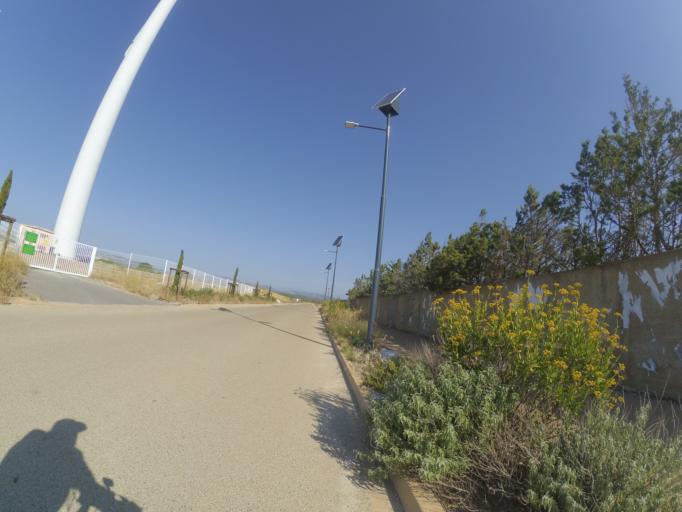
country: FR
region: Languedoc-Roussillon
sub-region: Departement des Pyrenees-Orientales
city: Salses-le-Chateau
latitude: 42.8053
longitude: 2.8920
